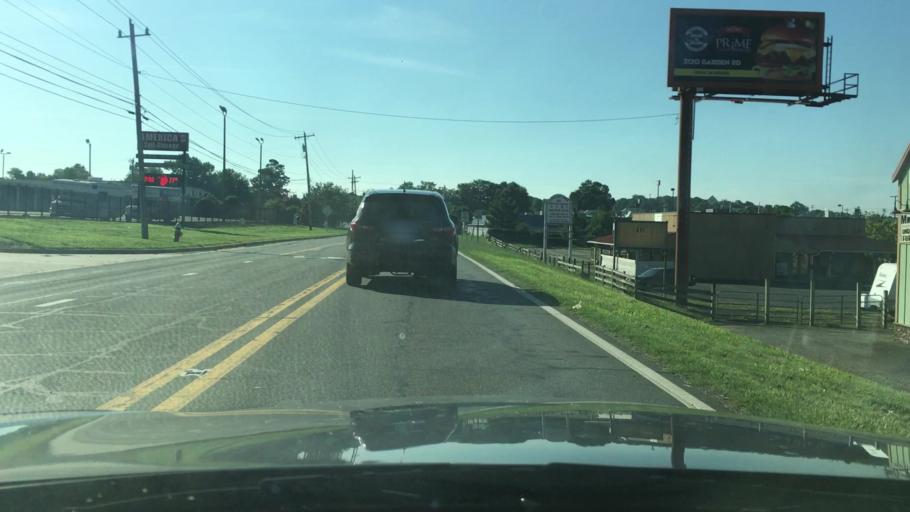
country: US
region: North Carolina
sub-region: Alamance County
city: Burlington
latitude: 36.0692
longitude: -79.4332
